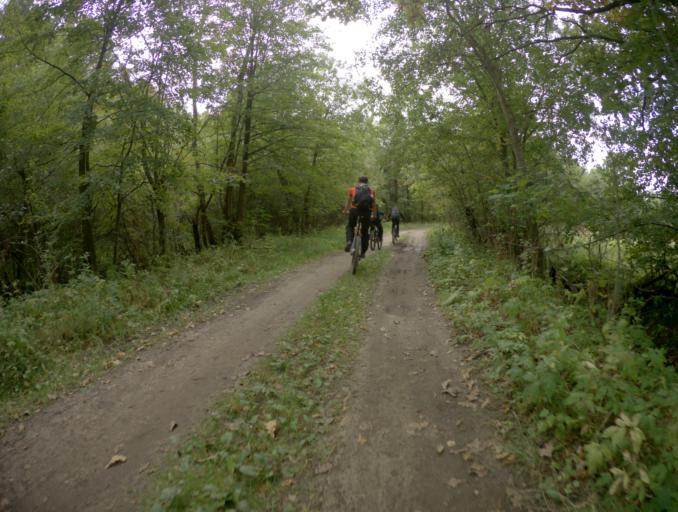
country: RU
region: Vladimir
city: Raduzhnyy
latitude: 56.0911
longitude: 40.2717
